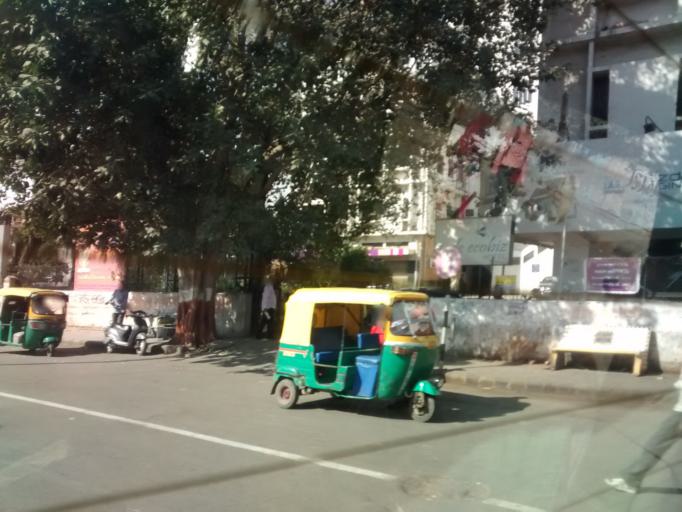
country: IN
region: Gujarat
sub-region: Ahmadabad
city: Ahmedabad
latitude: 23.0405
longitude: 72.5694
